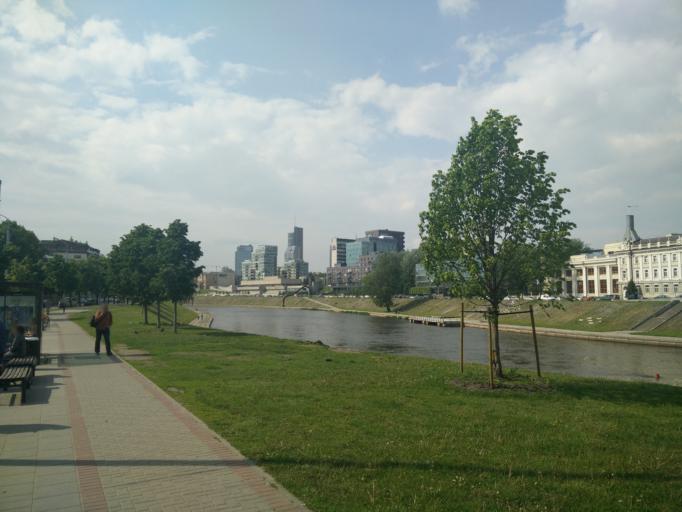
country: LT
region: Vilnius County
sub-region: Vilnius
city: Vilnius
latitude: 54.6885
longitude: 25.2878
